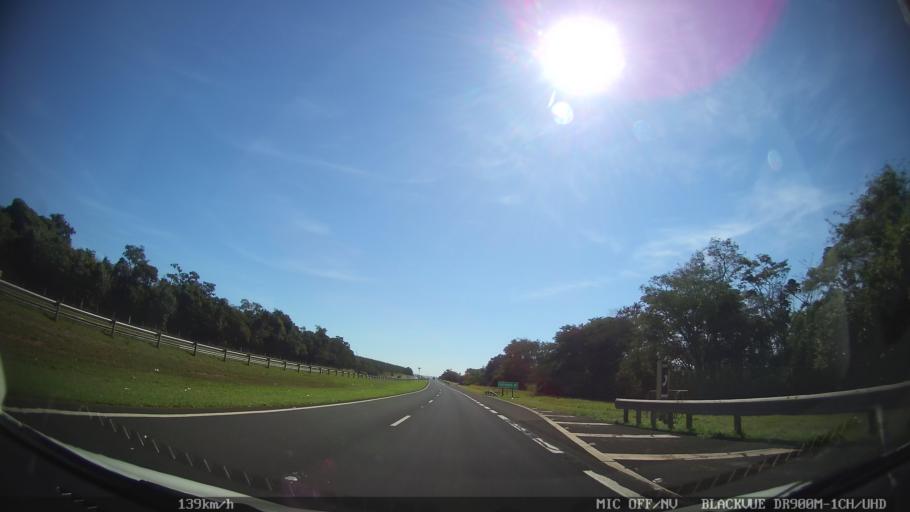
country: BR
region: Sao Paulo
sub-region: Sao Simao
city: Sao Simao
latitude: -21.6133
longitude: -47.6164
